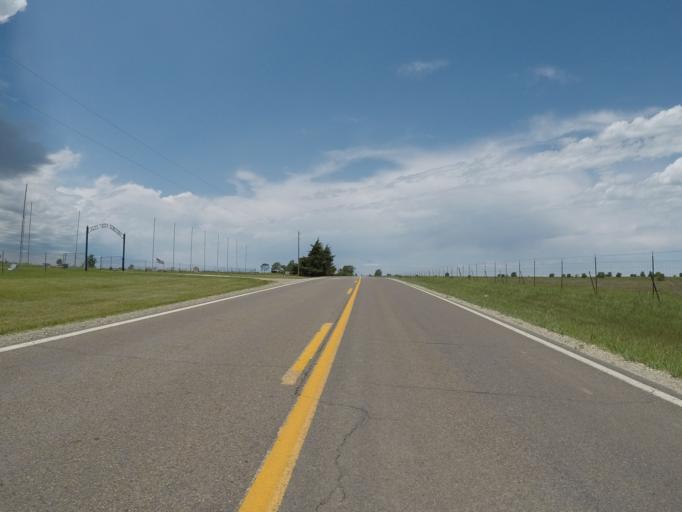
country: US
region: Kansas
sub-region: Morris County
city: Council Grove
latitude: 38.8551
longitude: -96.4649
